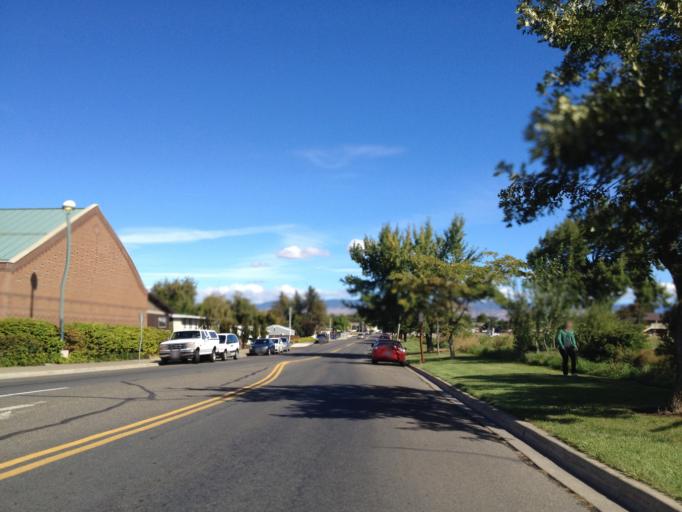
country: US
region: Washington
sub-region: Kittitas County
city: Ellensburg
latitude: 47.0062
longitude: -120.5433
